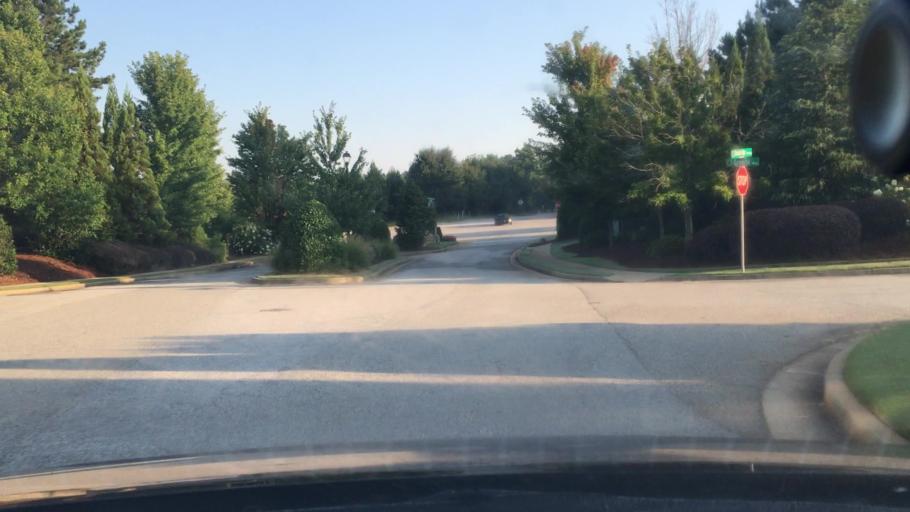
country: US
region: Georgia
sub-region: Coweta County
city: East Newnan
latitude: 33.3858
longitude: -84.7502
